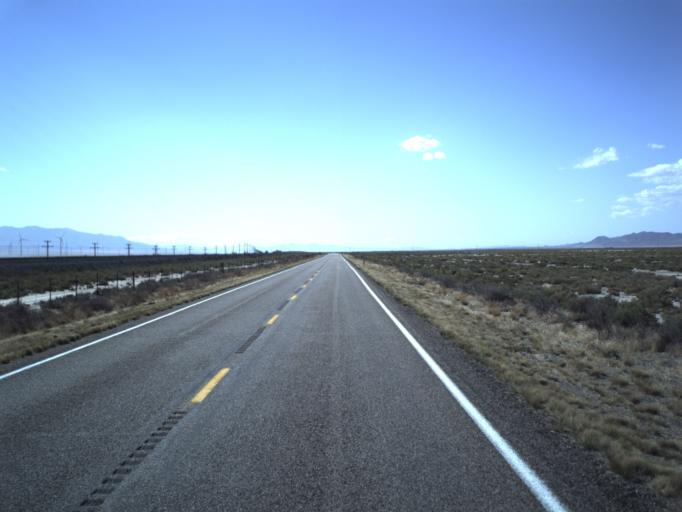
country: US
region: Utah
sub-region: Beaver County
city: Milford
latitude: 38.6170
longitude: -112.9855
